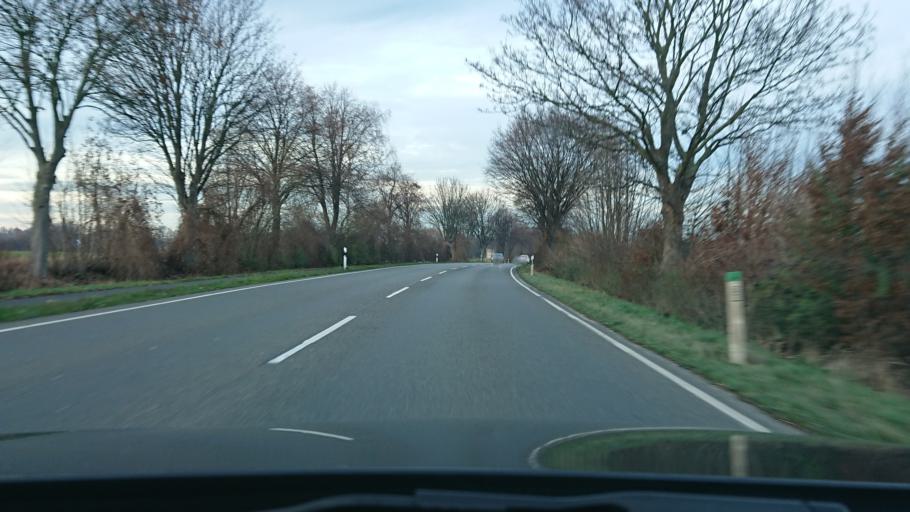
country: DE
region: North Rhine-Westphalia
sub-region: Regierungsbezirk Koln
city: Frechen
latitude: 50.9493
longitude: 6.8039
